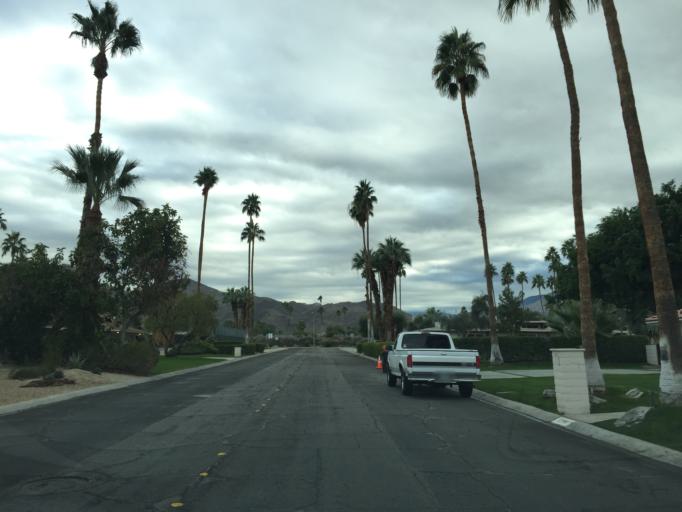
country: US
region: California
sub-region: Riverside County
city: Palm Springs
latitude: 33.7826
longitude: -116.5384
